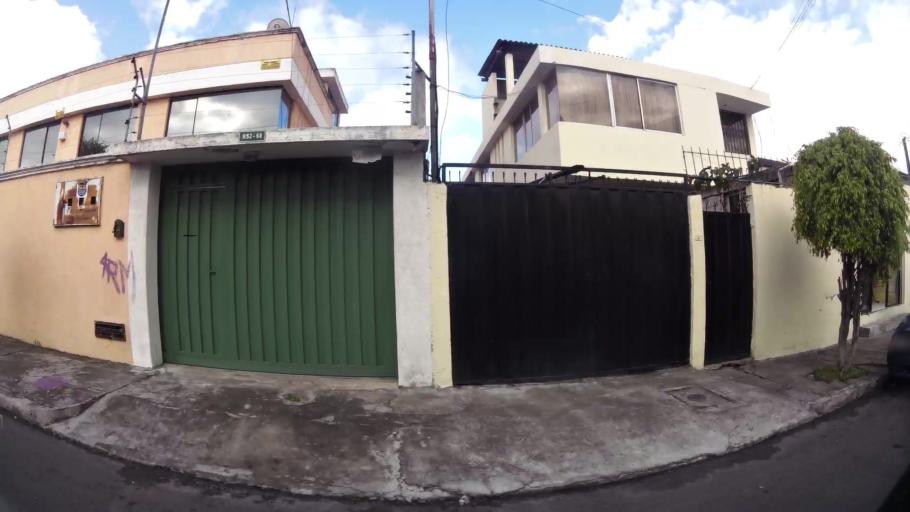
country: EC
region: Pichincha
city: Quito
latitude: -0.1416
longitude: -78.4722
